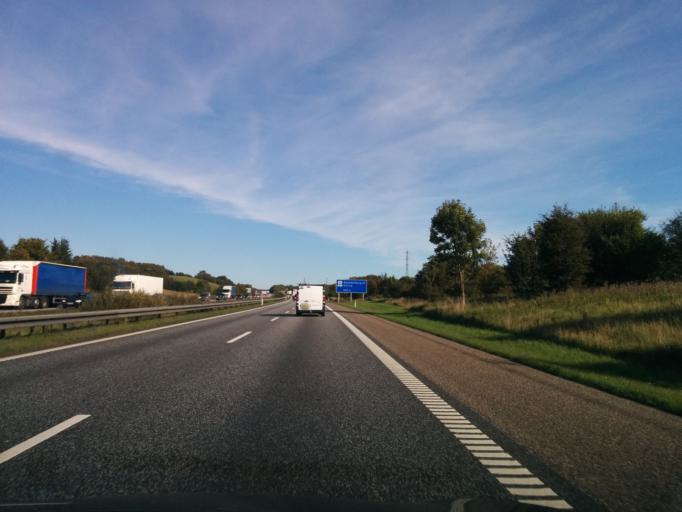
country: DK
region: Central Jutland
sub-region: Skanderborg Kommune
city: Stilling
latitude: 56.0592
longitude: 9.9618
